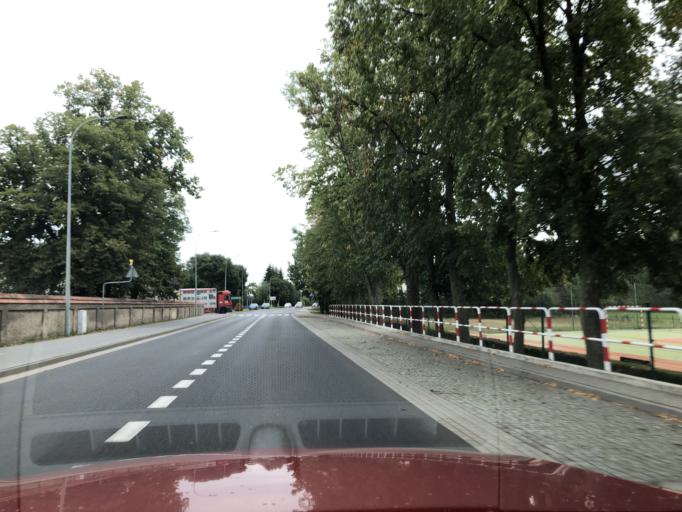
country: PL
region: Greater Poland Voivodeship
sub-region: Powiat szamotulski
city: Pniewy
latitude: 52.5160
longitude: 16.2469
